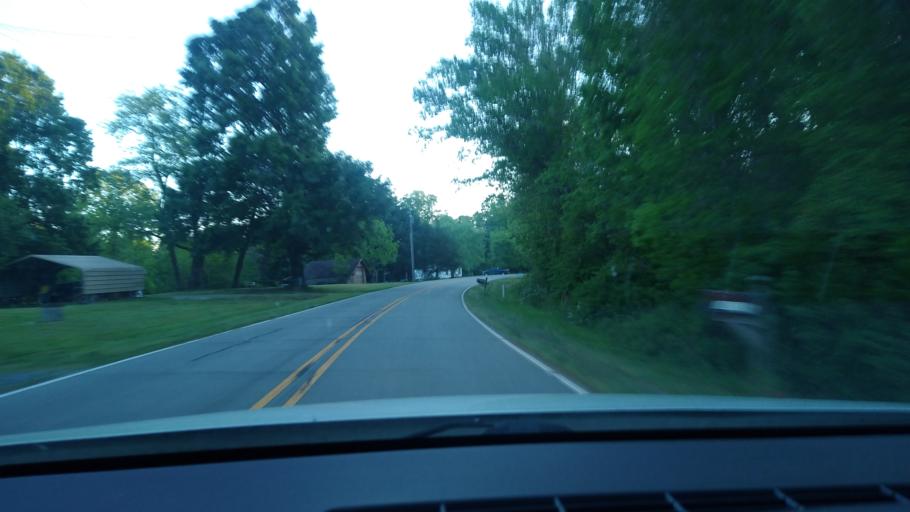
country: US
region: North Carolina
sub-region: Rockingham County
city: Reidsville
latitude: 36.3643
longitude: -79.5544
